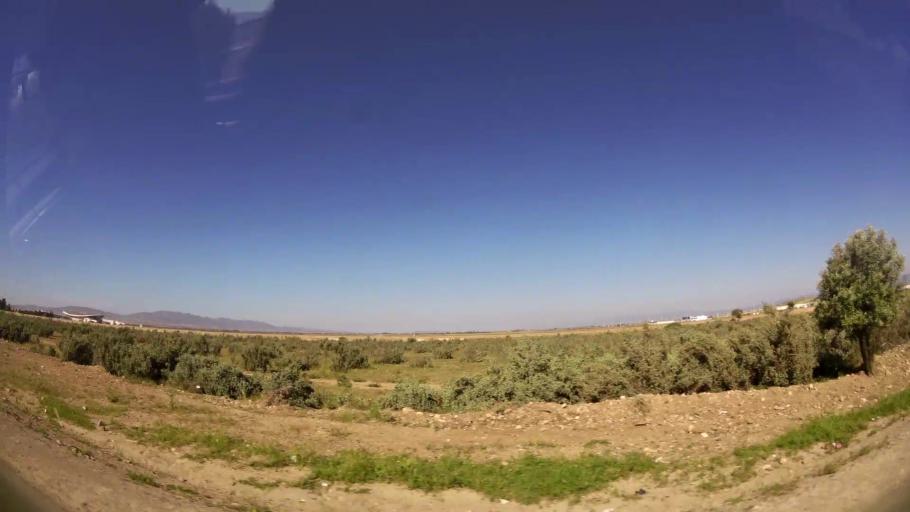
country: MA
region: Oriental
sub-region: Oujda-Angad
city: Oujda
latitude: 34.7758
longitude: -1.9447
